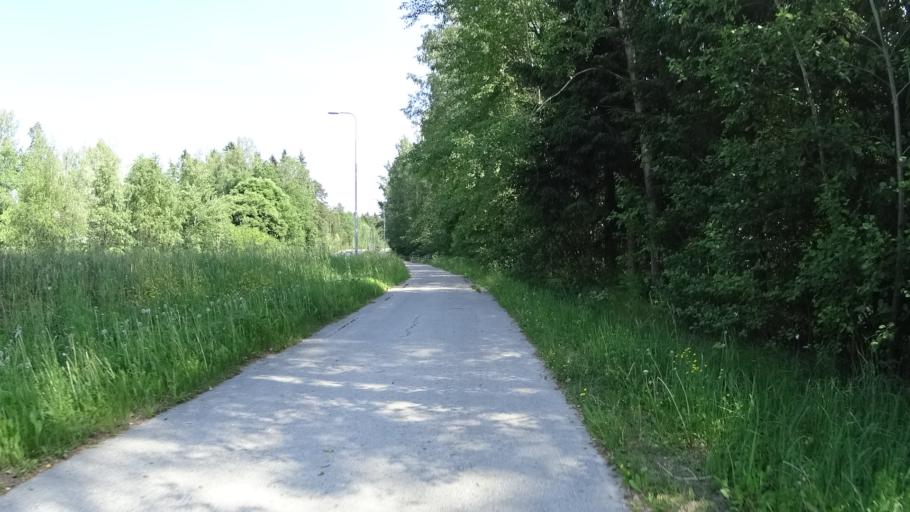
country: FI
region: Uusimaa
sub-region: Raaseporin
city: Karis
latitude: 60.0800
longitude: 23.6659
